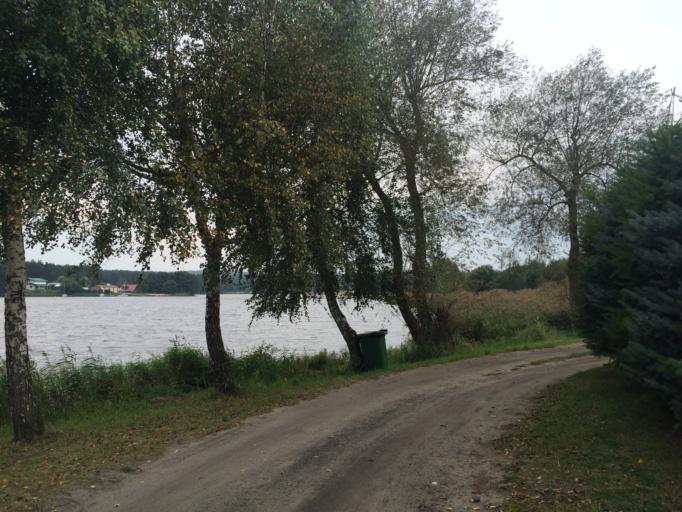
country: PL
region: Swietokrzyskie
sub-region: Powiat starachowicki
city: Starachowice
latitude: 51.0264
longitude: 21.0506
